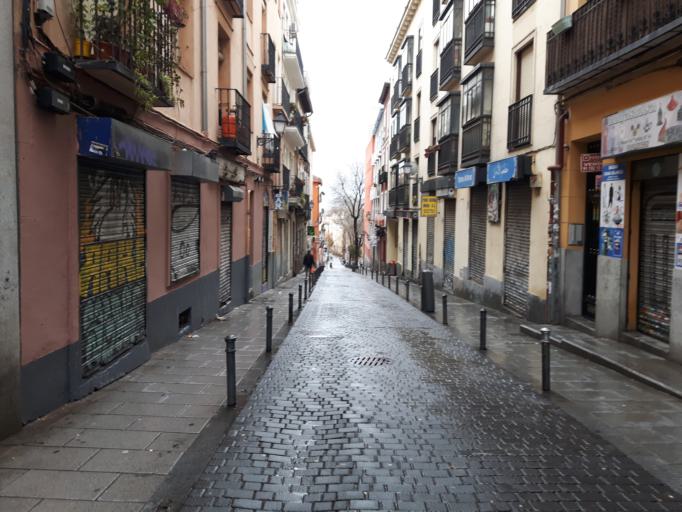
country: ES
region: Madrid
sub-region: Provincia de Madrid
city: Madrid
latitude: 40.4093
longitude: -3.7038
